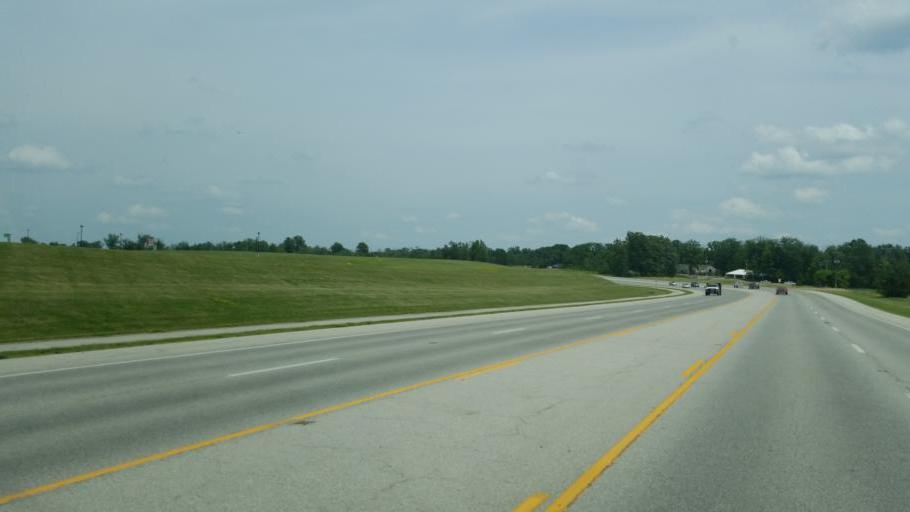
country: US
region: Ohio
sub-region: Delaware County
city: Powell
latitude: 40.1517
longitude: -83.1148
